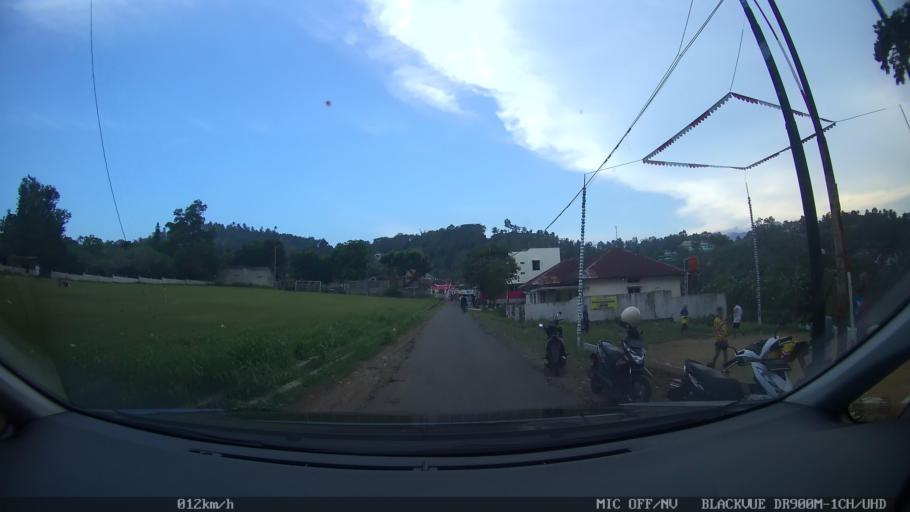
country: ID
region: Lampung
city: Bandarlampung
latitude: -5.4037
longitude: 105.2150
